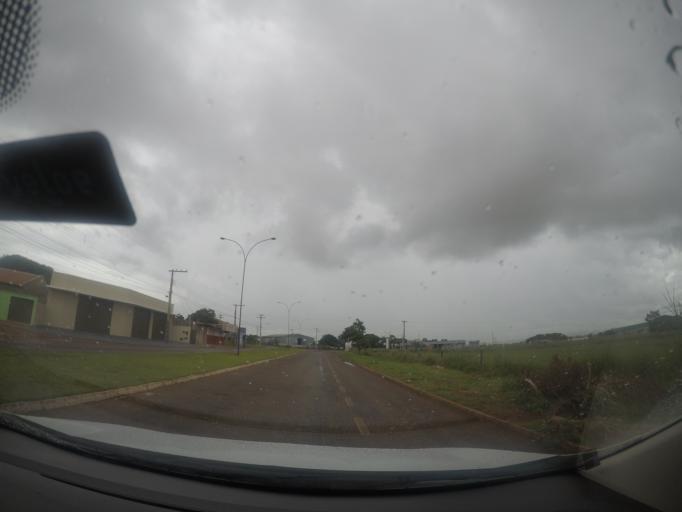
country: BR
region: Goias
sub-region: Trindade
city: Trindade
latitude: -16.6383
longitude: -49.4116
